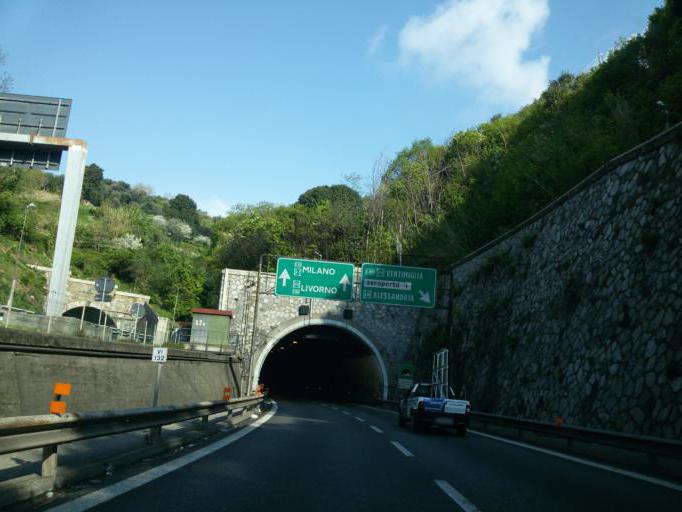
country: IT
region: Liguria
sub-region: Provincia di Genova
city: San Teodoro
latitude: 44.4189
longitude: 8.9018
